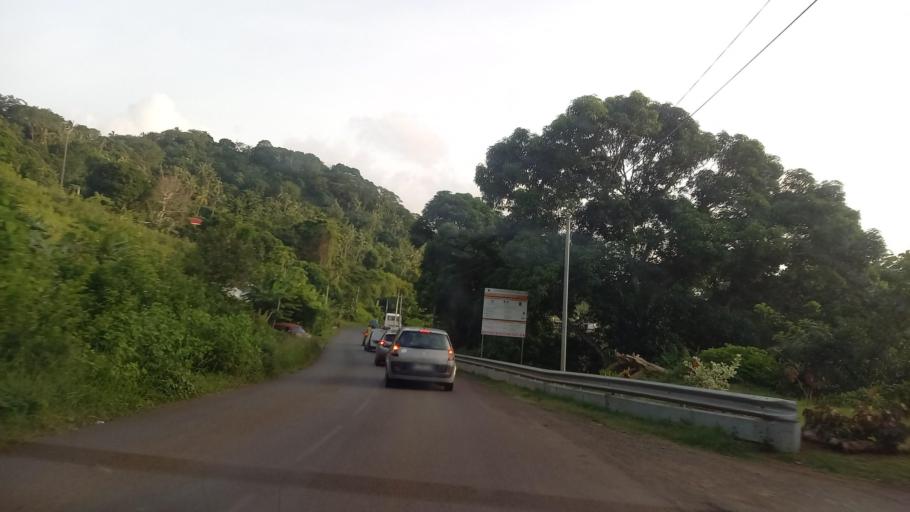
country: YT
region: M'Tsangamouji
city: M'Tsangamouji
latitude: -12.7558
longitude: 45.0895
